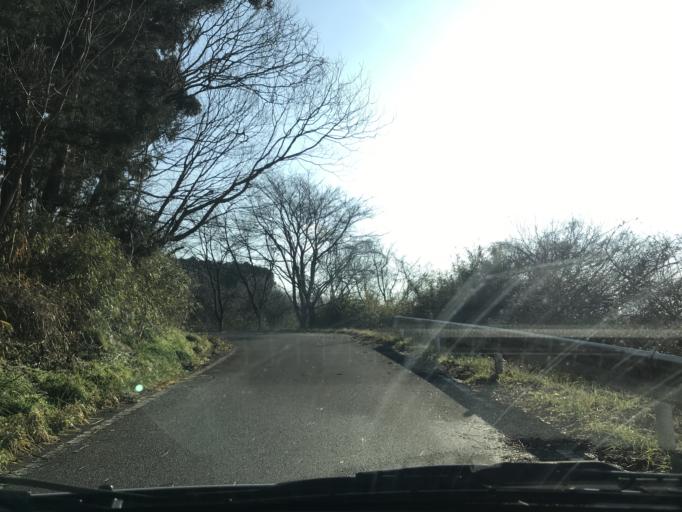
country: JP
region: Miyagi
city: Wakuya
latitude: 38.6863
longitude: 141.1281
